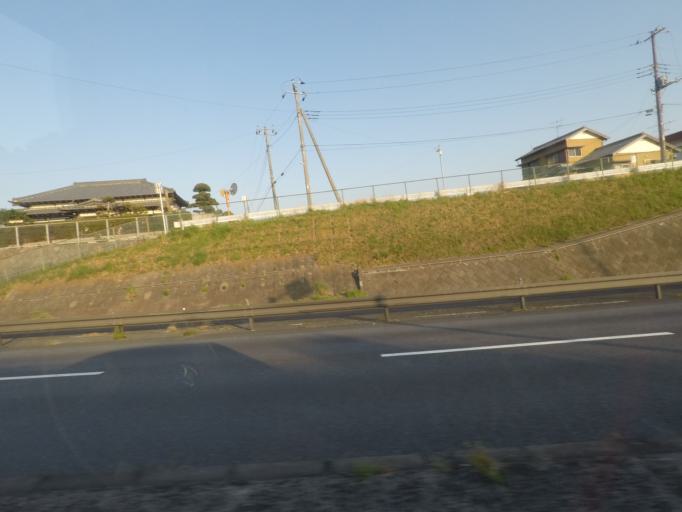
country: JP
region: Chiba
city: Shisui
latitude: 35.7230
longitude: 140.2677
